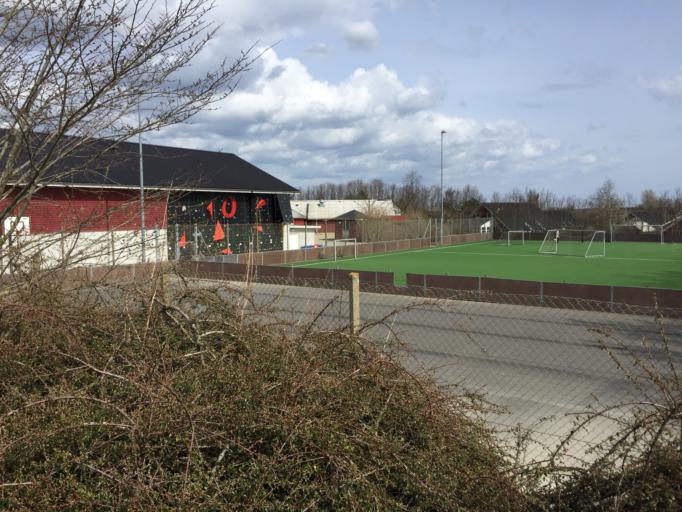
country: DK
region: South Denmark
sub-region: Svendborg Kommune
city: Thuro By
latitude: 55.1162
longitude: 10.7238
